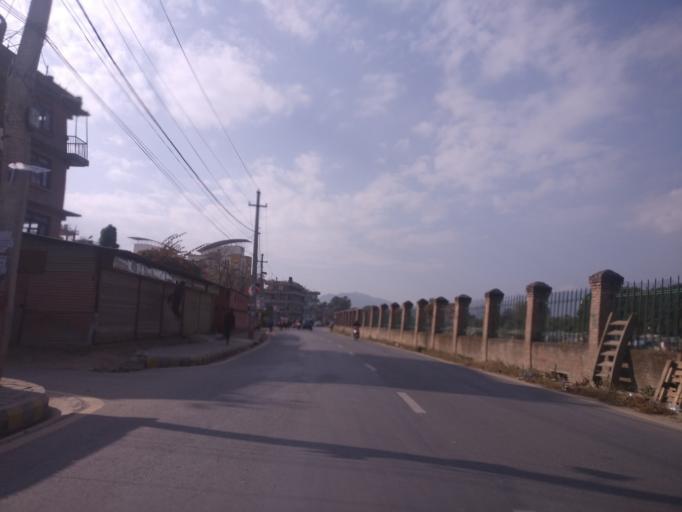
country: NP
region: Central Region
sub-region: Bagmati Zone
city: Patan
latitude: 27.6863
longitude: 85.3226
